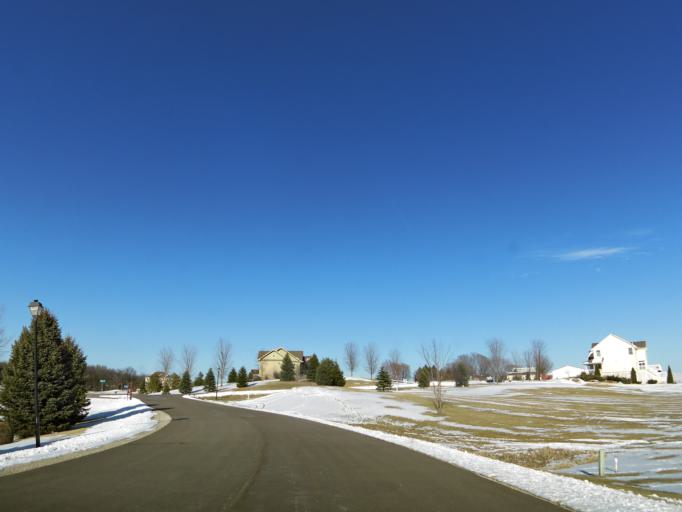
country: US
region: Minnesota
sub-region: Scott County
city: Elko New Market
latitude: 44.6325
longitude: -93.3849
